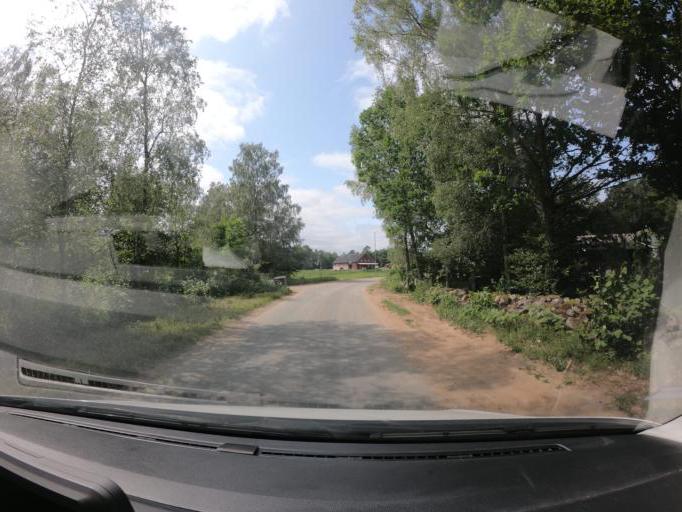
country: SE
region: Skane
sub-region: Hassleholms Kommun
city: Sosdala
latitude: 56.1095
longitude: 13.6360
